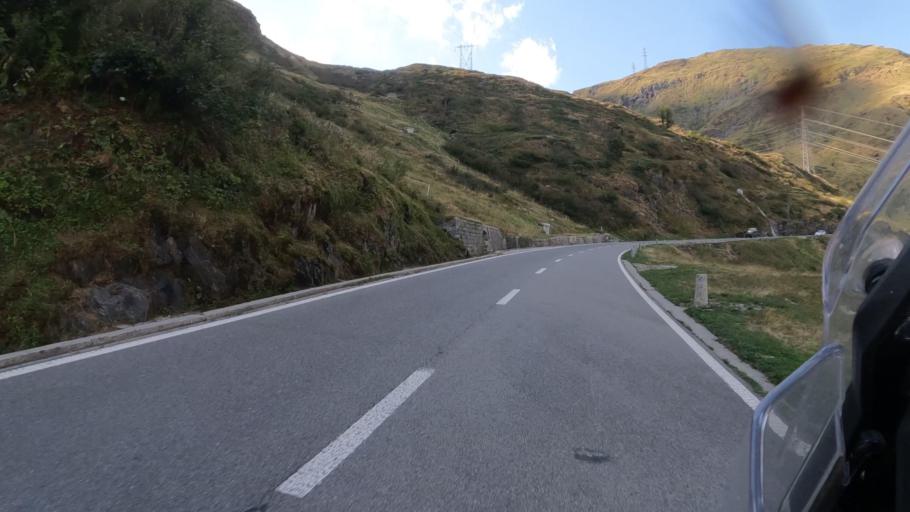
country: CH
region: Ticino
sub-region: Leventina District
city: Airolo
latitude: 46.5369
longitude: 8.5793
